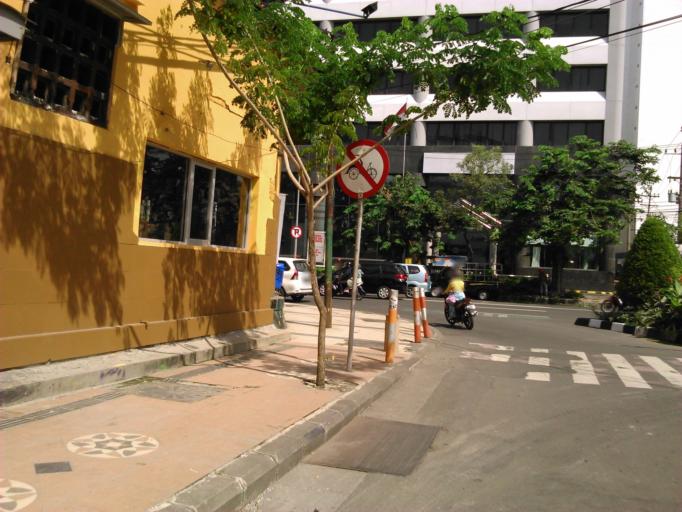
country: ID
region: East Java
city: Gubengairlangga
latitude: -7.2720
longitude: 112.7432
